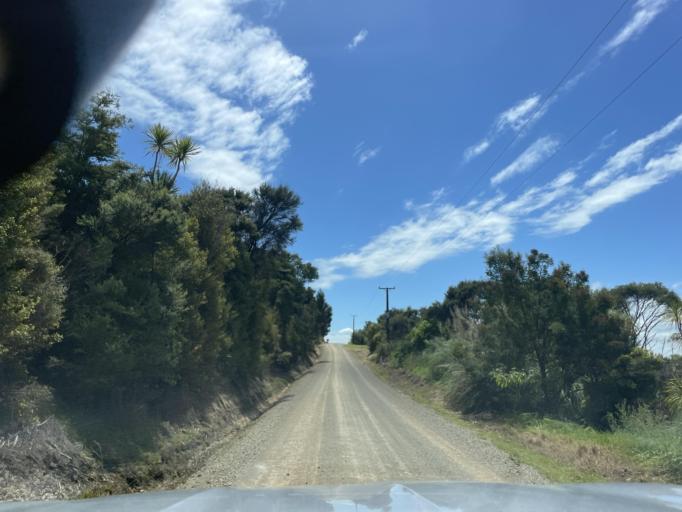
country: NZ
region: Auckland
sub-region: Auckland
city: Wellsford
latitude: -36.2164
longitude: 174.3547
